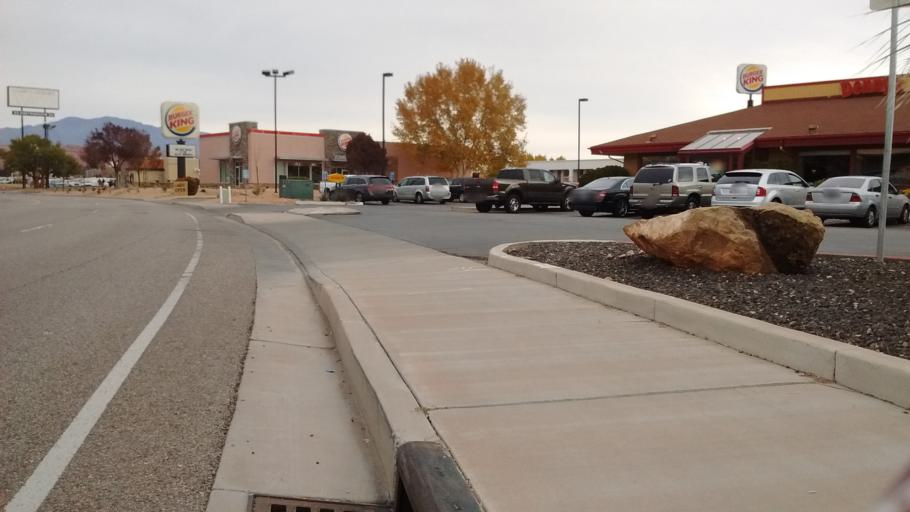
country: US
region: Utah
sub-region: Washington County
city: Saint George
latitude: 37.0873
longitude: -113.5836
